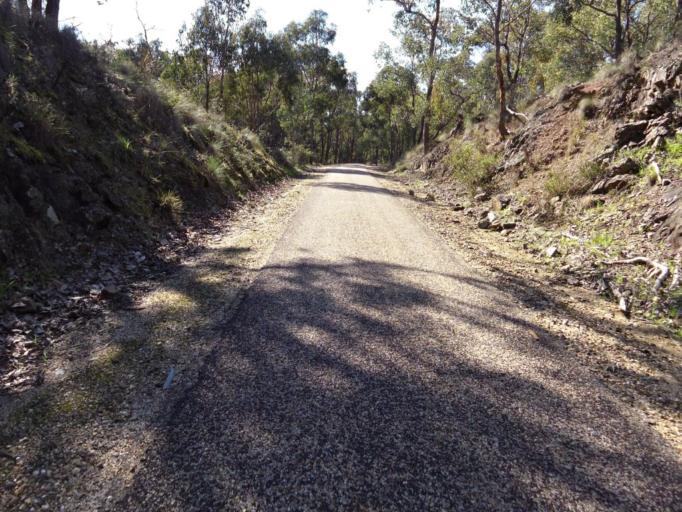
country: AU
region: Victoria
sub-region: Wangaratta
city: Wangaratta
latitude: -36.4061
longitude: 146.6211
